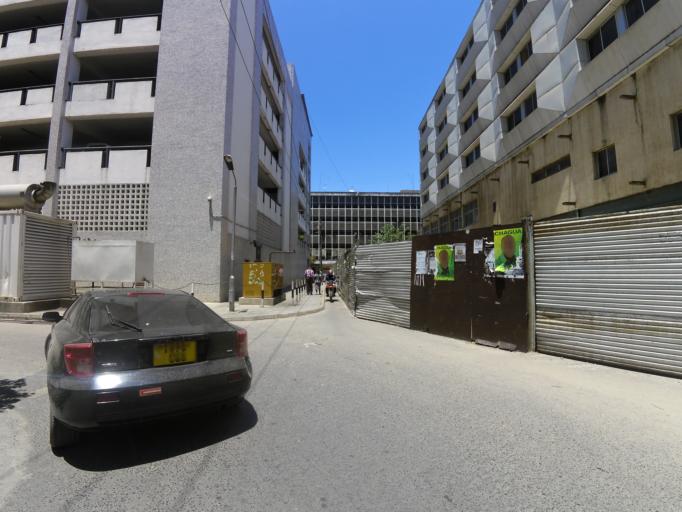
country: TZ
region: Dar es Salaam
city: Dar es Salaam
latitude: -6.8145
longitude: 39.2889
